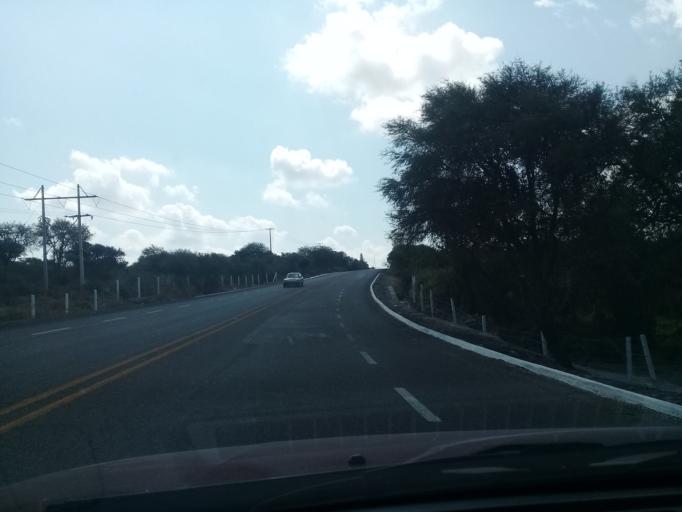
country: MX
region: Aguascalientes
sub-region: Aguascalientes
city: Penuelas (El Cienegal)
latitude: 21.7597
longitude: -102.3506
